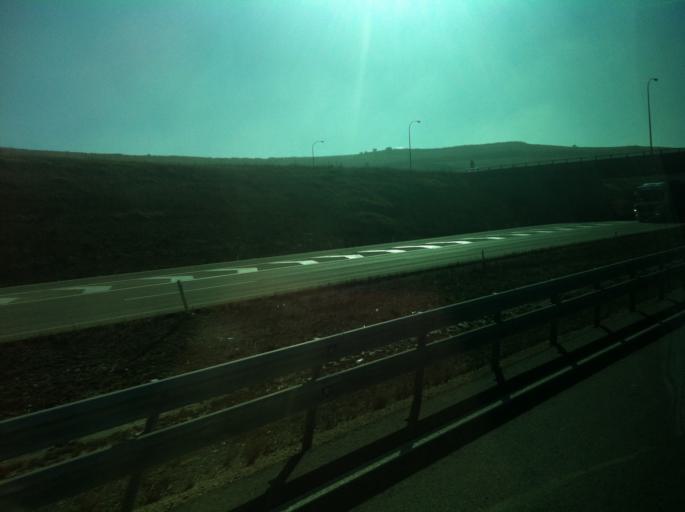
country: ES
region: Castille and Leon
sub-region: Provincia de Burgos
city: Rubena
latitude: 42.3787
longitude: -3.5839
